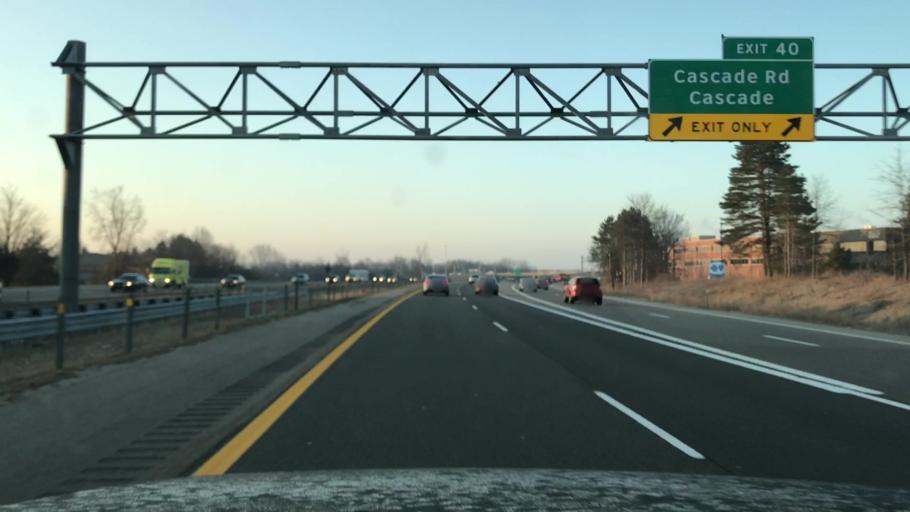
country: US
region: Michigan
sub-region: Kent County
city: East Grand Rapids
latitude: 42.9523
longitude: -85.5683
